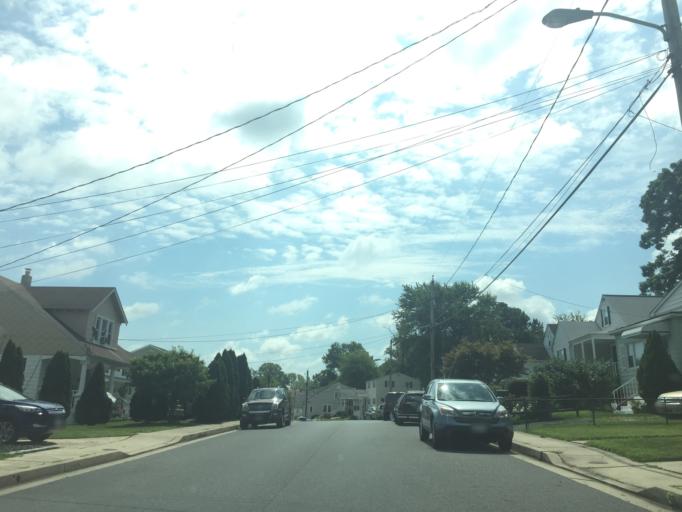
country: US
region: Maryland
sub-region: Baltimore County
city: Carney
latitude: 39.3848
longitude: -76.5279
